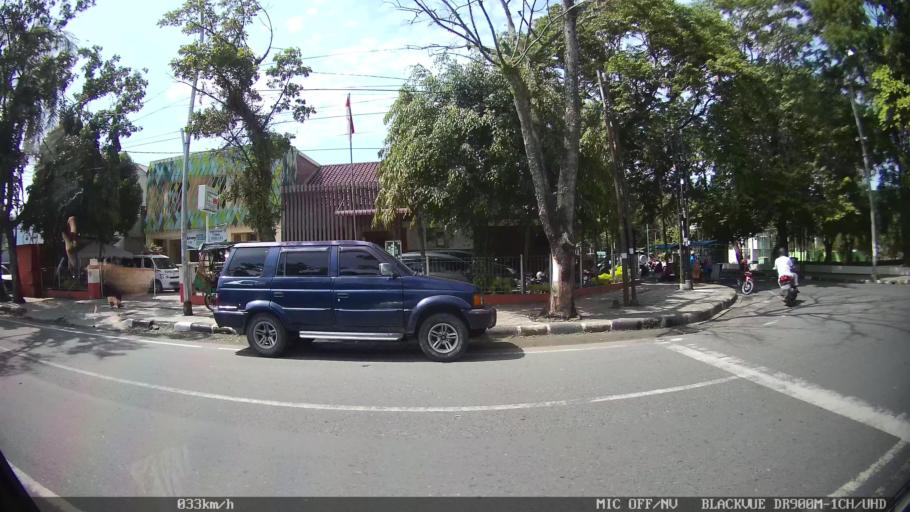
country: ID
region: North Sumatra
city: Medan
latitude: 3.5847
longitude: 98.6590
